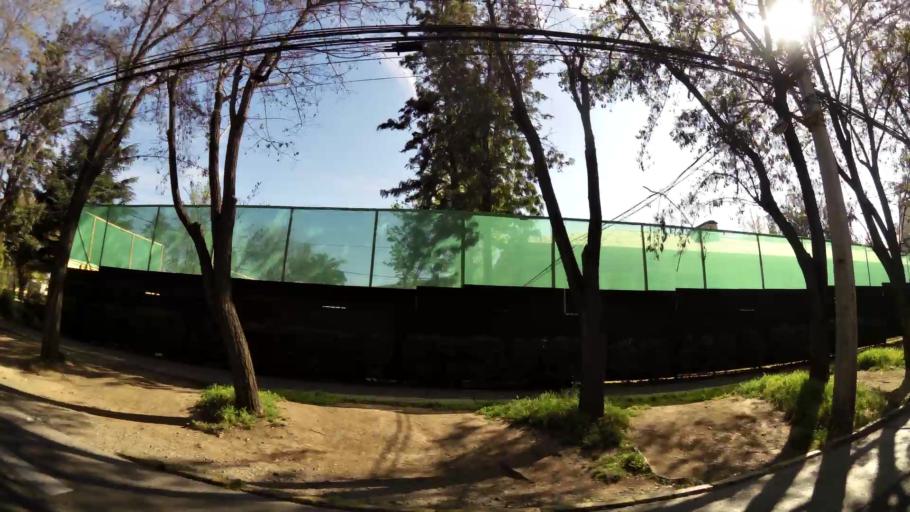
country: CL
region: Santiago Metropolitan
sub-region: Provincia de Santiago
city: Villa Presidente Frei, Nunoa, Santiago, Chile
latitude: -33.4382
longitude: -70.5682
